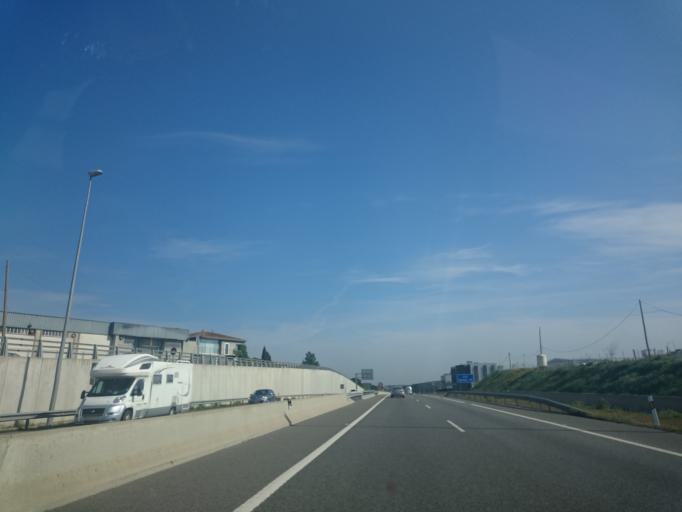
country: ES
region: Catalonia
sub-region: Provincia de Girona
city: Riudellots de la Selva
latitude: 41.8997
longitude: 2.7865
